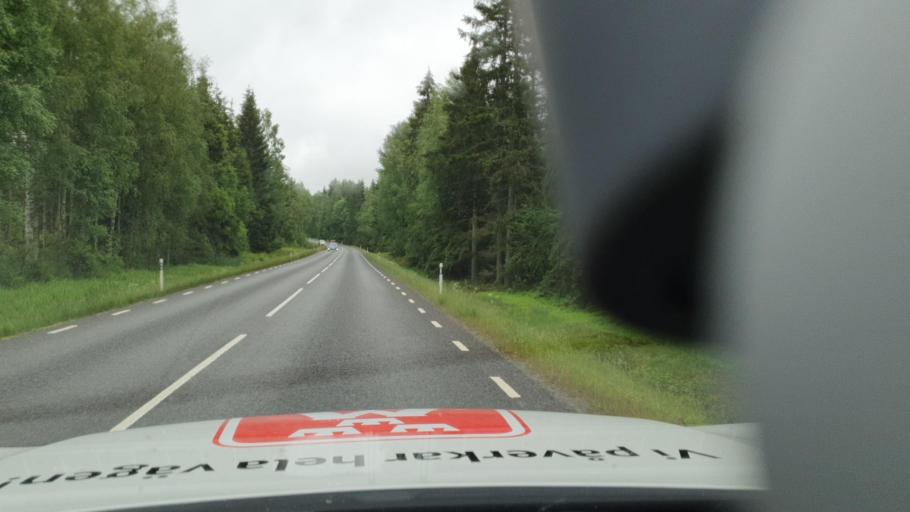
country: SE
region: Vaermland
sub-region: Kristinehamns Kommun
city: Bjorneborg
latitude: 59.2201
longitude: 14.3172
